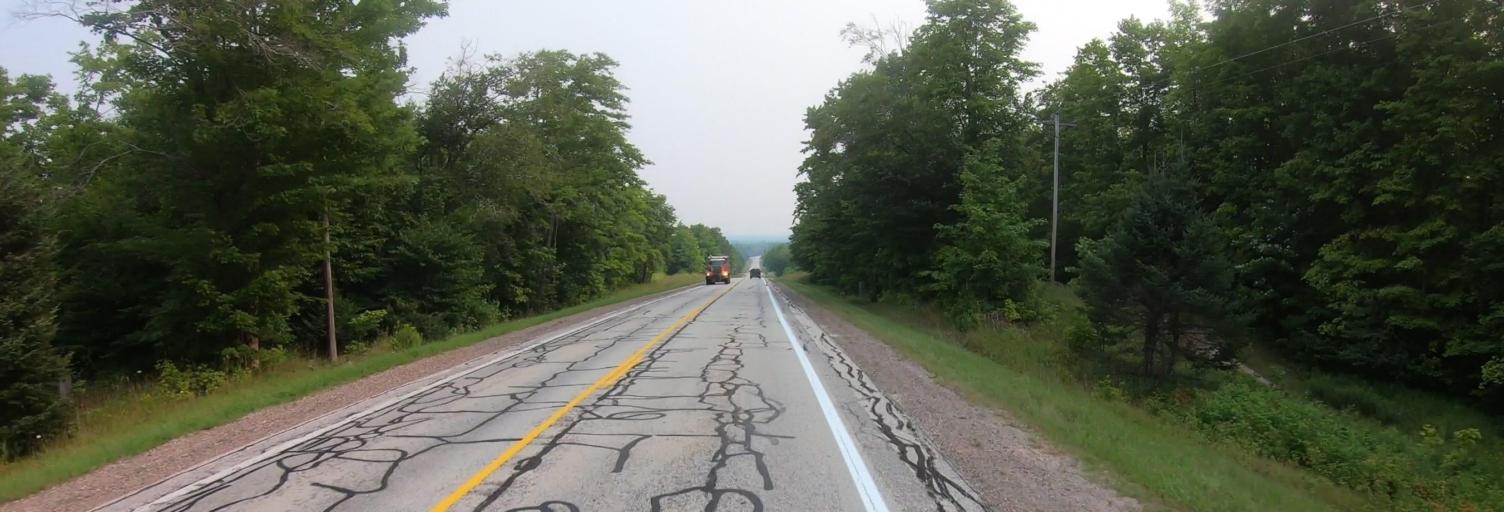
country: US
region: Michigan
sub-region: Luce County
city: Newberry
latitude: 46.4975
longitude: -85.0959
